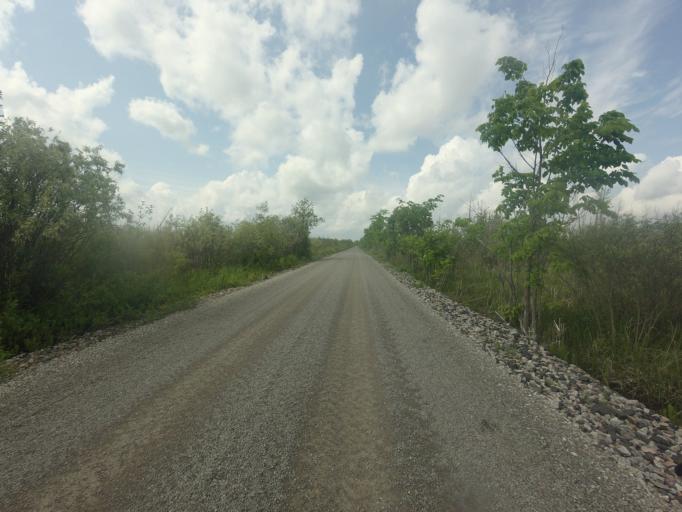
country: CA
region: Ontario
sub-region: Lanark County
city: Smiths Falls
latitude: 45.0074
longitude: -76.0695
